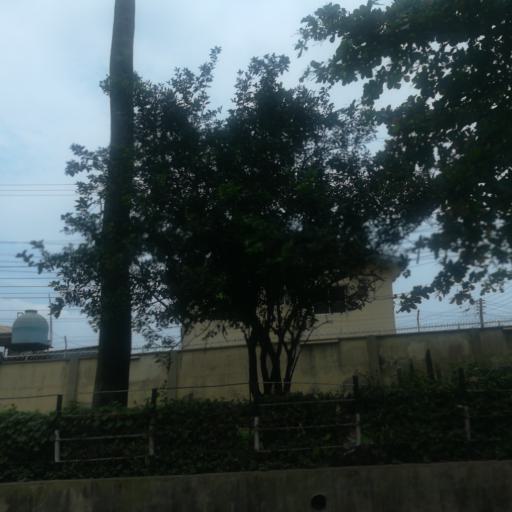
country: NG
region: Lagos
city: Ojota
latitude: 6.5791
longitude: 3.3854
